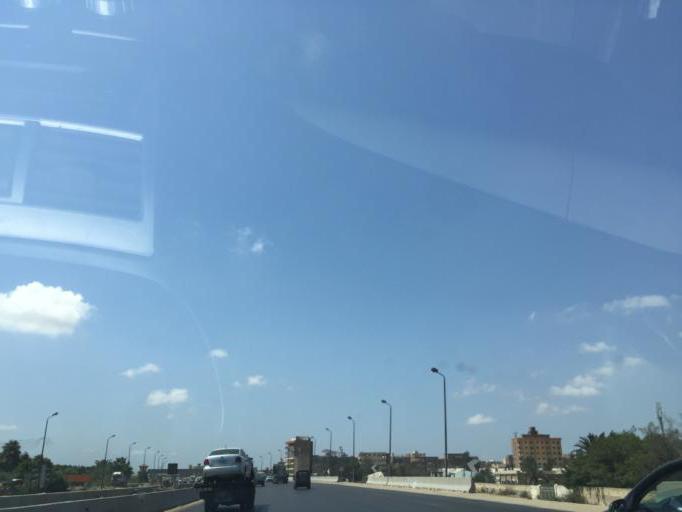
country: EG
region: Alexandria
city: Alexandria
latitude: 31.0018
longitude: 29.8068
